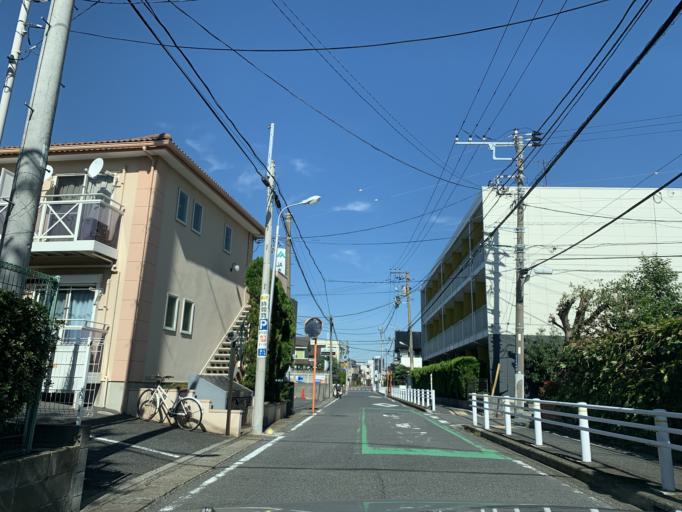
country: JP
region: Tokyo
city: Urayasu
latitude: 35.6582
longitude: 139.8929
